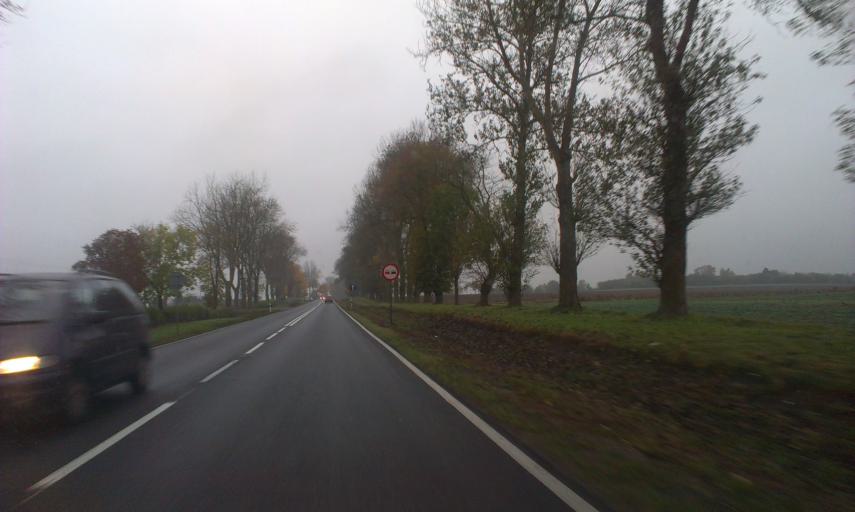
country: PL
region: West Pomeranian Voivodeship
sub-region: Koszalin
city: Koszalin
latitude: 54.1551
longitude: 16.2348
